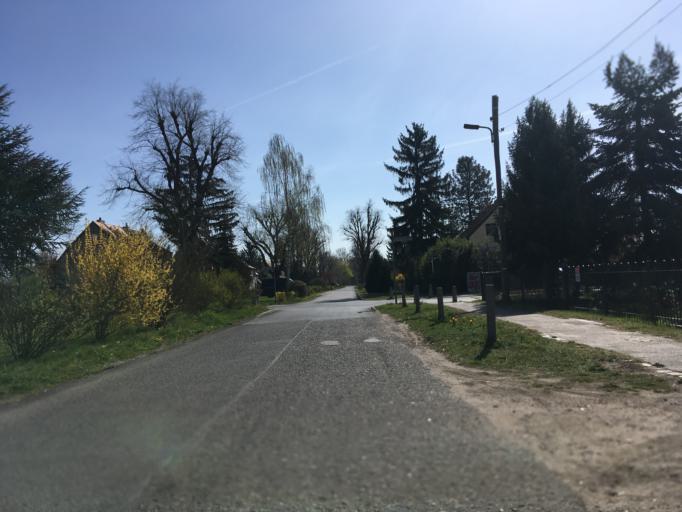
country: DE
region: Berlin
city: Kaulsdorf
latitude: 52.5070
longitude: 13.5992
